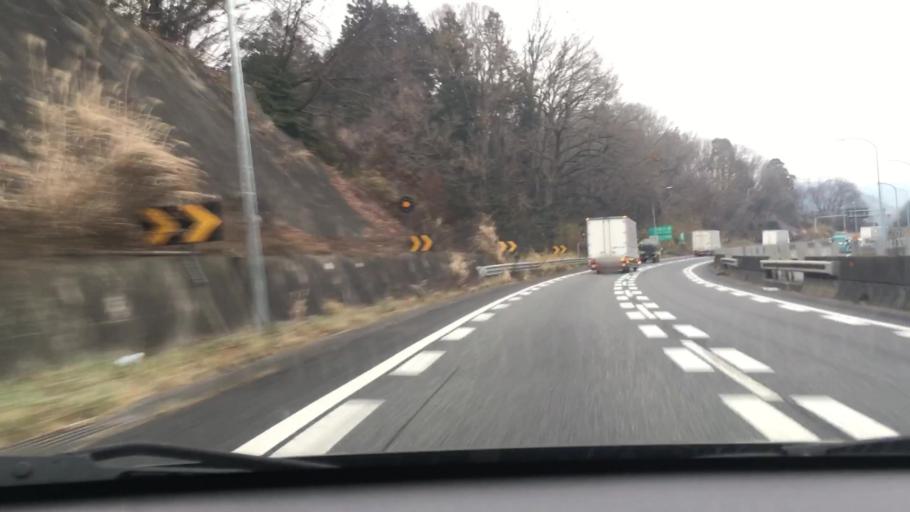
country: JP
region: Mie
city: Nabari
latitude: 34.6890
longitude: 136.0479
